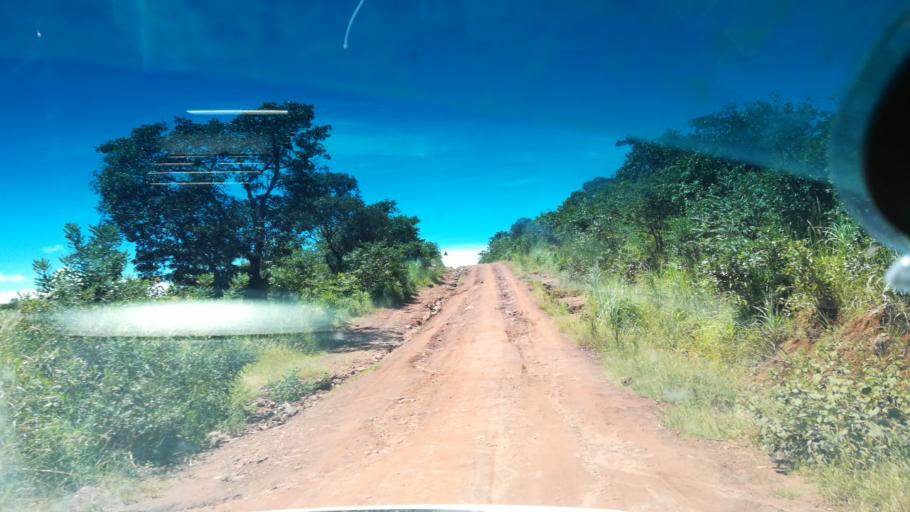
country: ZM
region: Luapula
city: Nchelenge
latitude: -8.7047
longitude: 28.7009
